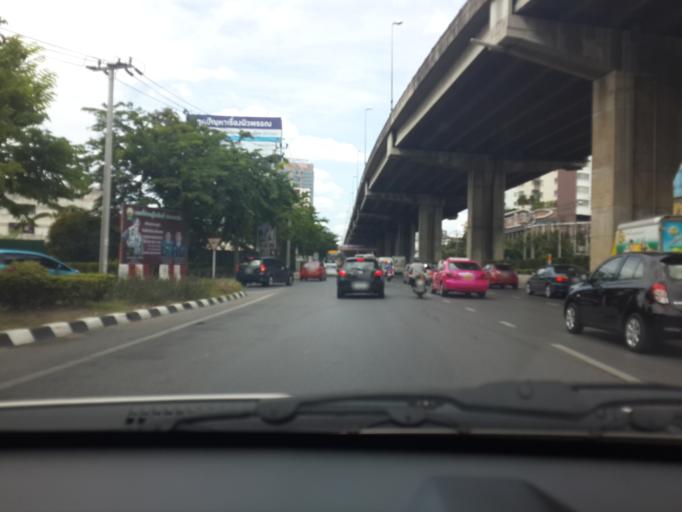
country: TH
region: Bangkok
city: Taling Chan
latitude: 13.7871
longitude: 100.4692
